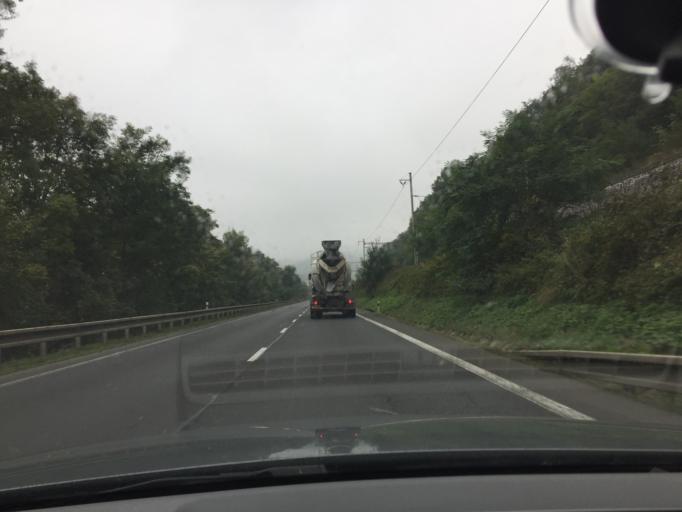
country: CZ
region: Ustecky
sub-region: Okres Usti nad Labem
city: Usti nad Labem
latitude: 50.6023
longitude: 14.0708
